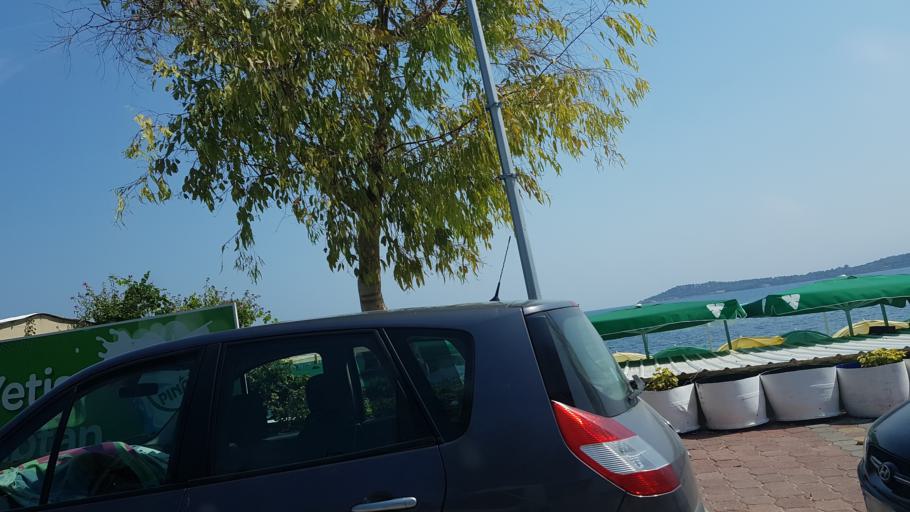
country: TR
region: Izmir
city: Urla
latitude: 38.3718
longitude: 26.7621
